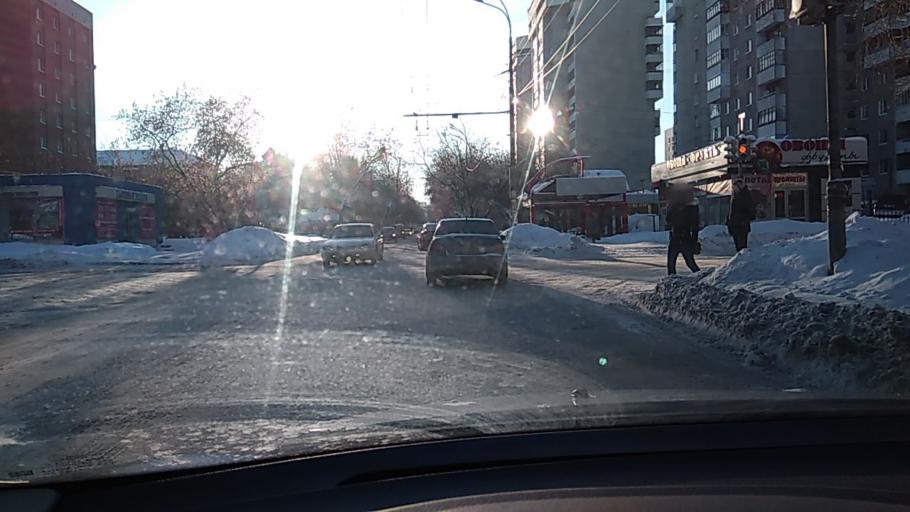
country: RU
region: Sverdlovsk
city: Yekaterinburg
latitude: 56.8922
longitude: 60.6010
